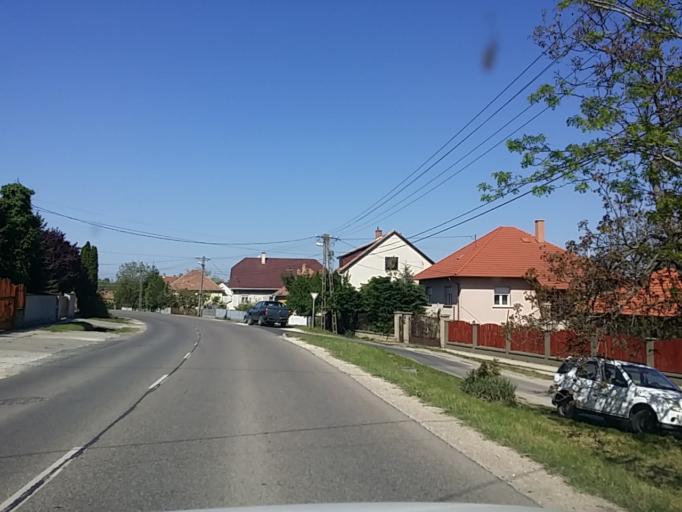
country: HU
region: Pest
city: Mogyorod
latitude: 47.6018
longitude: 19.2494
